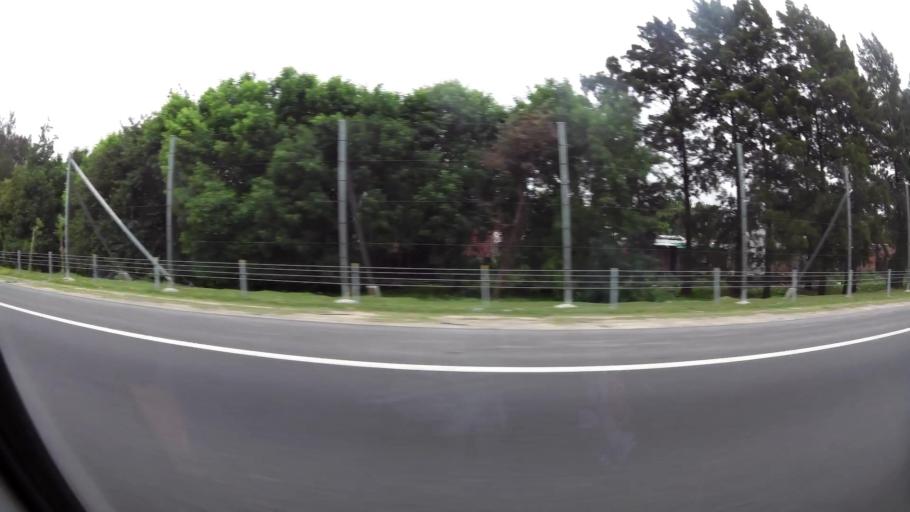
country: AR
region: Buenos Aires
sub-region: Partido de Quilmes
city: Quilmes
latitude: -34.7066
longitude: -58.2629
